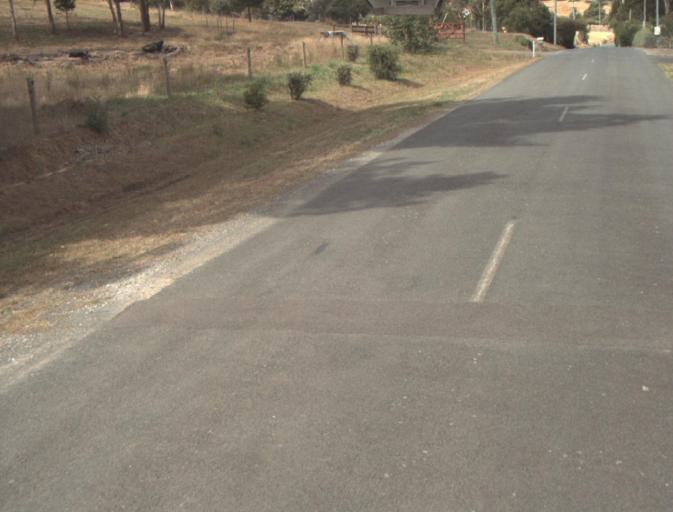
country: AU
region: Tasmania
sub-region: Launceston
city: Mayfield
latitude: -41.3146
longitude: 147.0209
